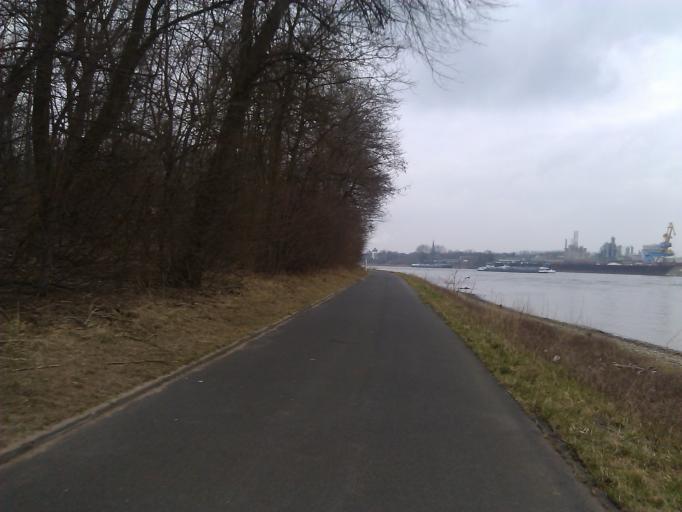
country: DE
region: North Rhine-Westphalia
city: Niederkassel
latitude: 50.8174
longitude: 7.0224
